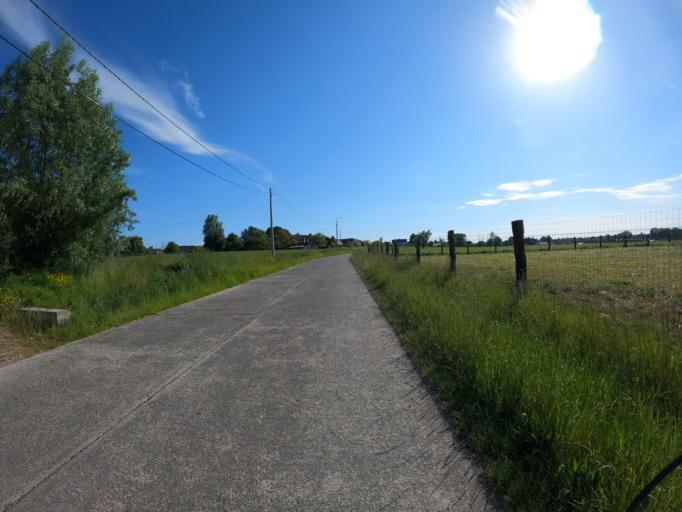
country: BE
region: Flanders
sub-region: Provincie Oost-Vlaanderen
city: Gavere
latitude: 50.9500
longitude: 3.6752
